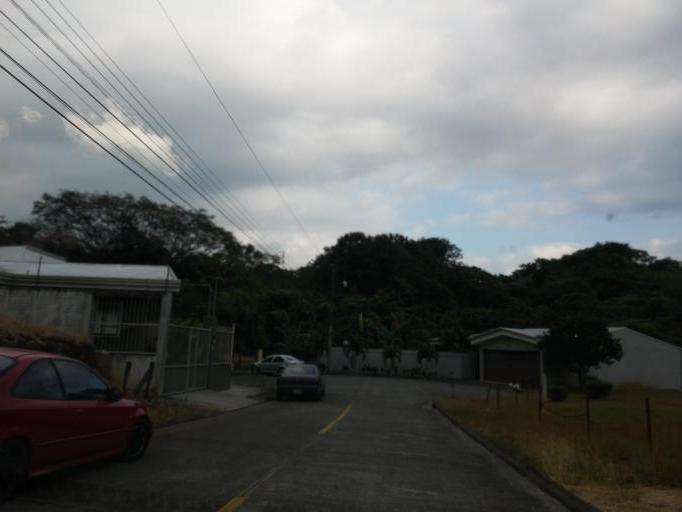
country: CR
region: Alajuela
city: Alajuela
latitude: 10.0277
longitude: -84.2106
